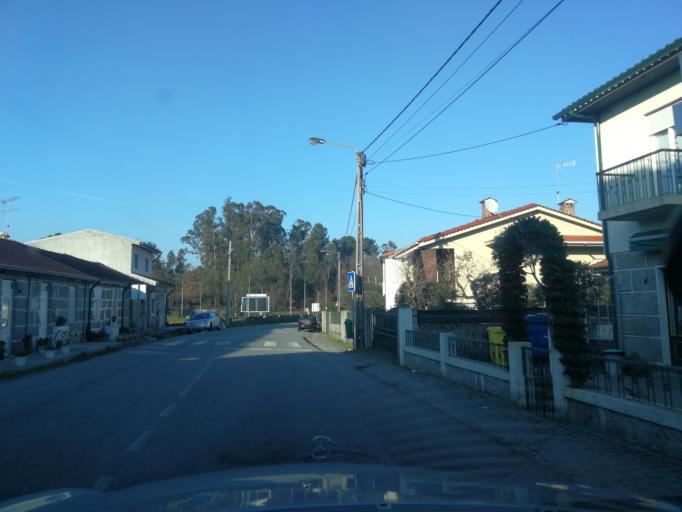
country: PT
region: Braga
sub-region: Guimaraes
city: Ponte
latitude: 41.4909
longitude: -8.3393
